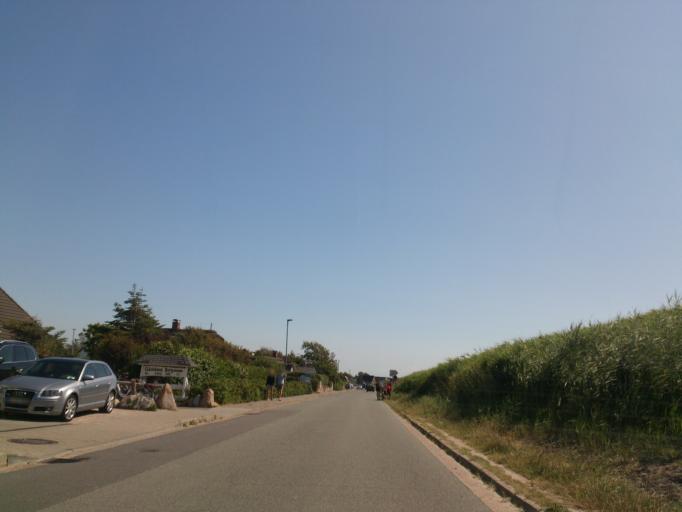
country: DE
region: Schleswig-Holstein
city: Sankt Peter-Ording
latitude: 54.3332
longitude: 8.6053
